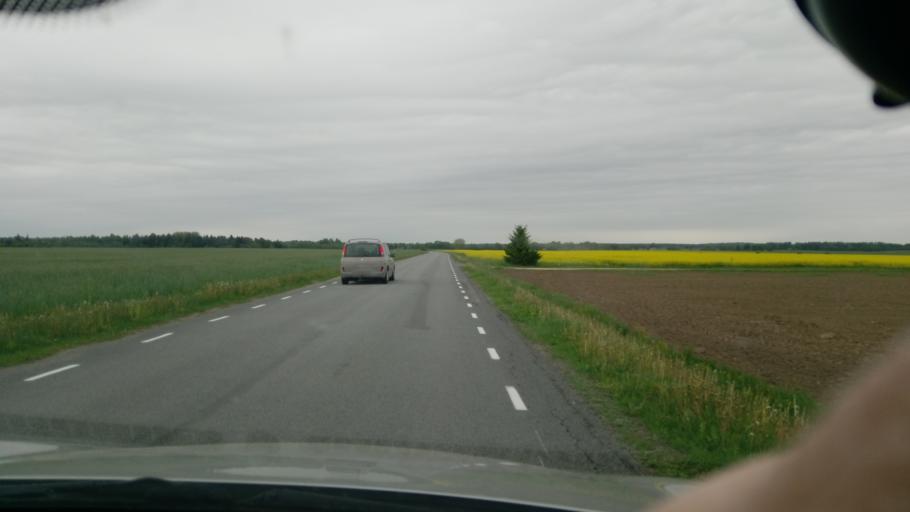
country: EE
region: Jaervamaa
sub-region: Koeru vald
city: Koeru
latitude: 58.9926
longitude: 26.0593
